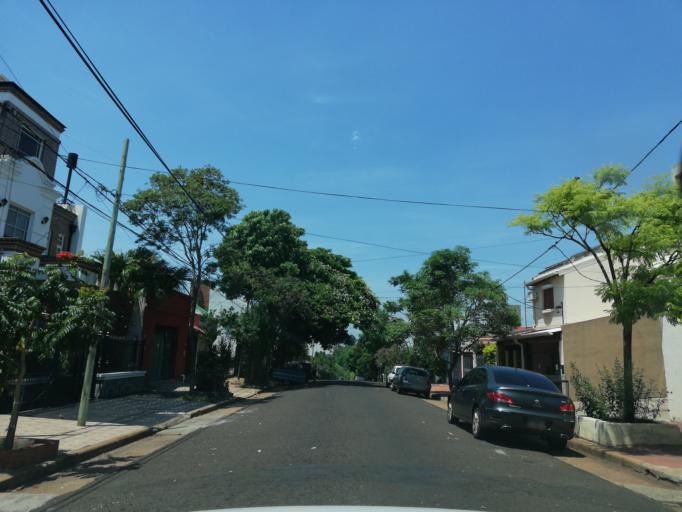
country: AR
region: Misiones
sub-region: Departamento de Capital
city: Posadas
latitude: -27.3569
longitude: -55.8986
